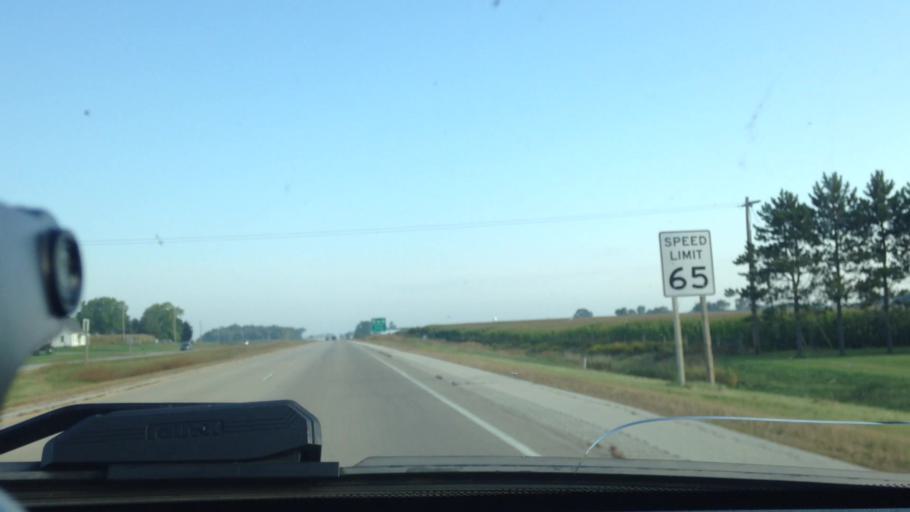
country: US
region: Wisconsin
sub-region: Oconto County
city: Oconto Falls
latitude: 45.0377
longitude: -88.0443
